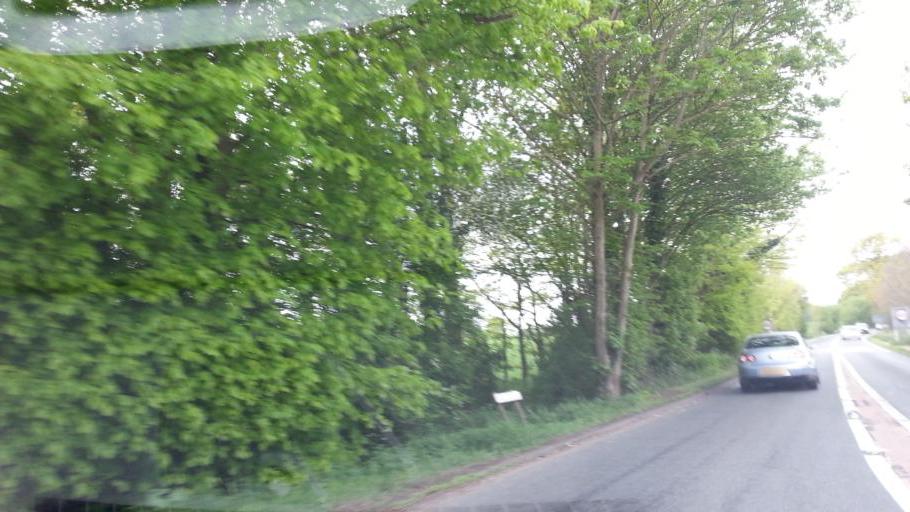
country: GB
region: England
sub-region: Suffolk
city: Capel Saint Mary
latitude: 52.0494
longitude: 1.0364
